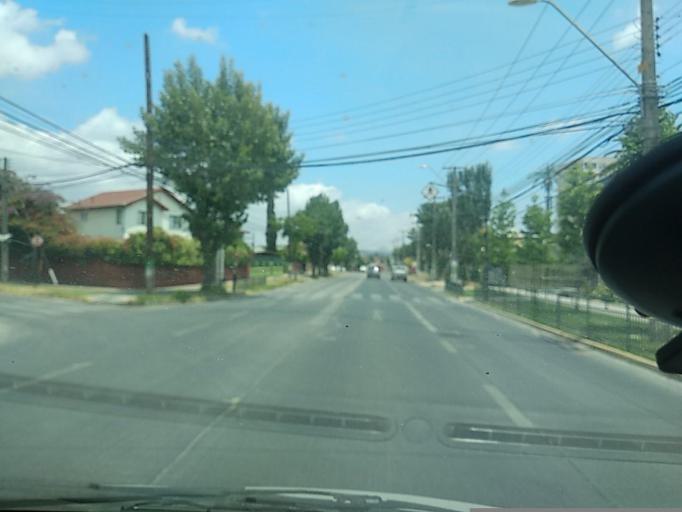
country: CL
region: Valparaiso
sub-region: Provincia de Marga Marga
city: Quilpue
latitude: -33.0430
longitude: -71.4327
